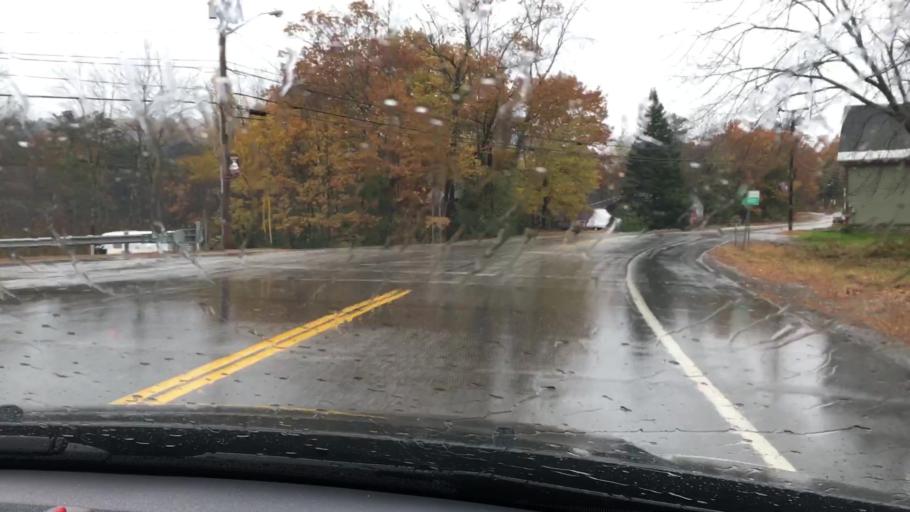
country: US
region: New Hampshire
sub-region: Grafton County
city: Ashland
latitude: 43.7041
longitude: -71.6303
